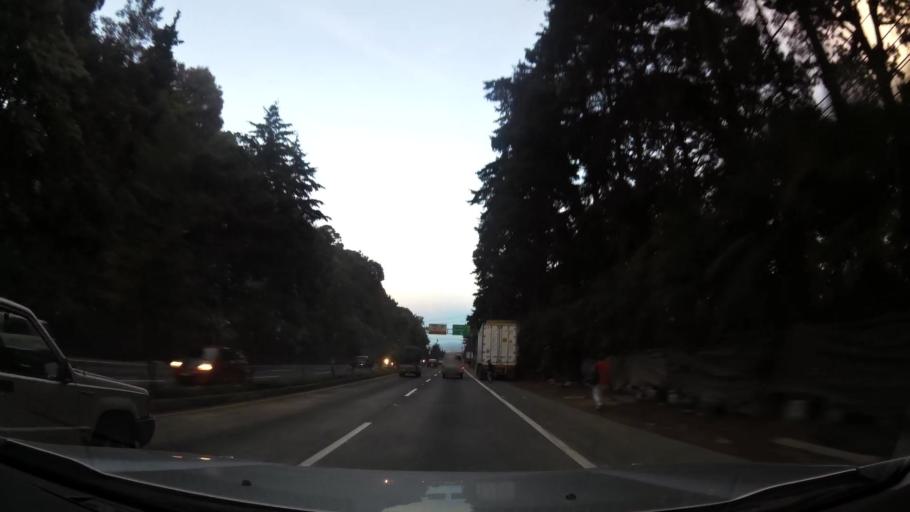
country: GT
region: Sacatepequez
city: San Lucas Sacatepequez
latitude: 14.5997
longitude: -90.6369
